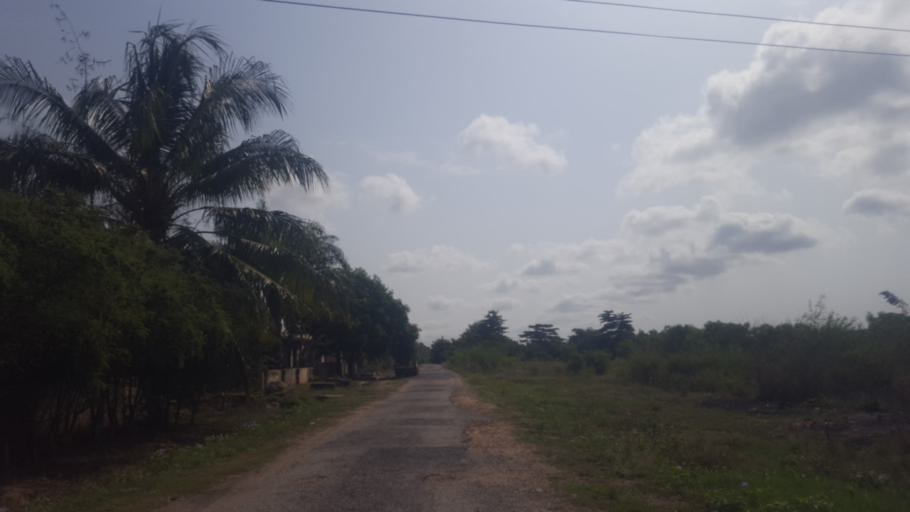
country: GH
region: Central
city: Winneba
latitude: 5.3683
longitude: -0.6437
